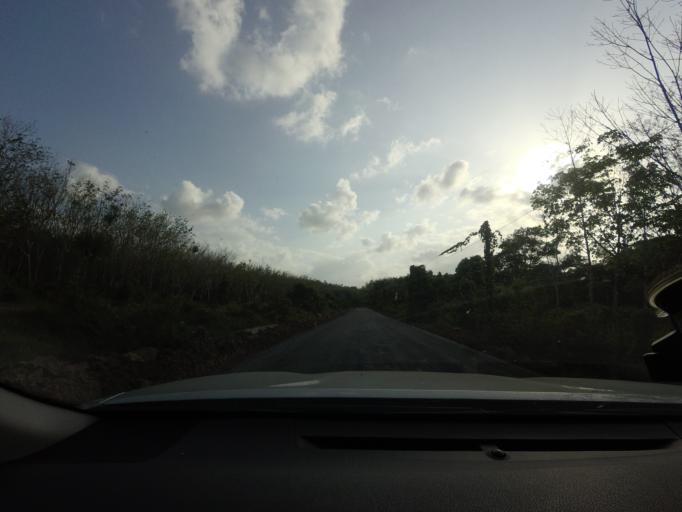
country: TH
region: Pattani
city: Mae Lan
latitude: 6.6175
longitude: 101.2458
